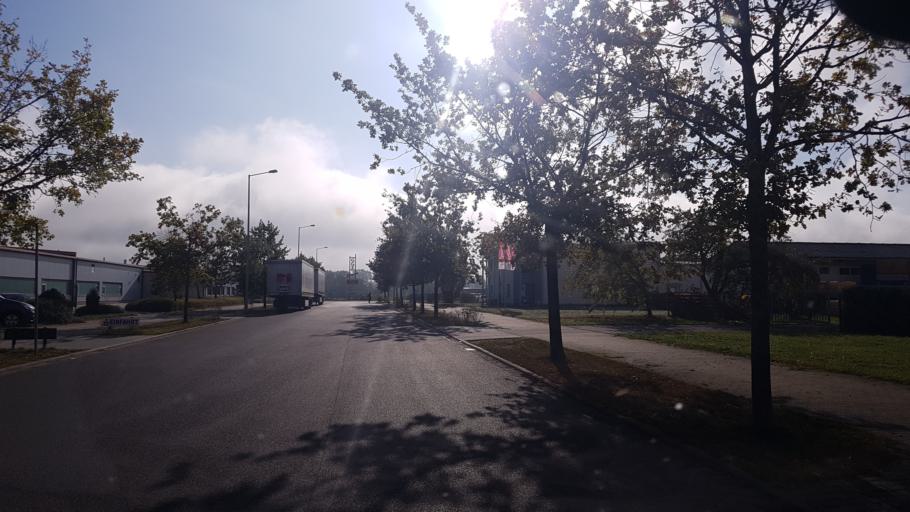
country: DE
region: Brandenburg
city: Elsterwerda
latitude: 51.4619
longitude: 13.5381
